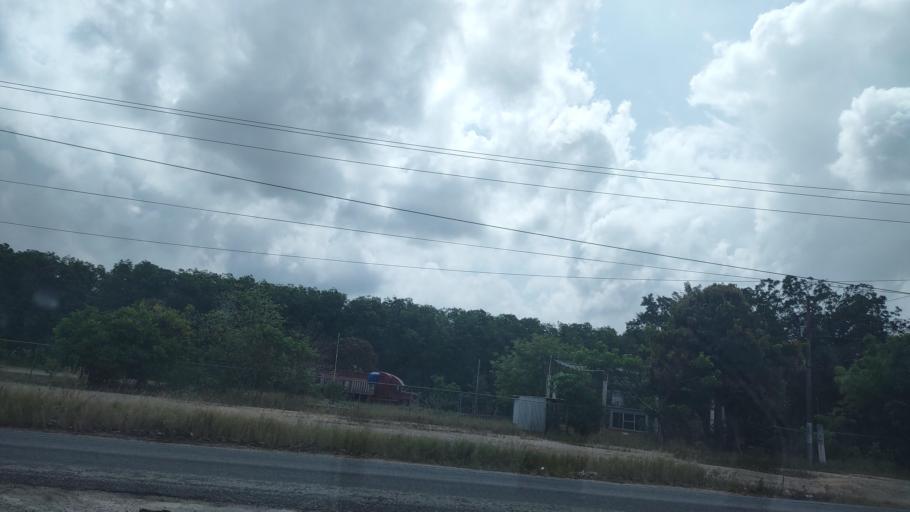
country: MX
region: Veracruz
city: Las Choapas
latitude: 17.9482
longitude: -94.1100
